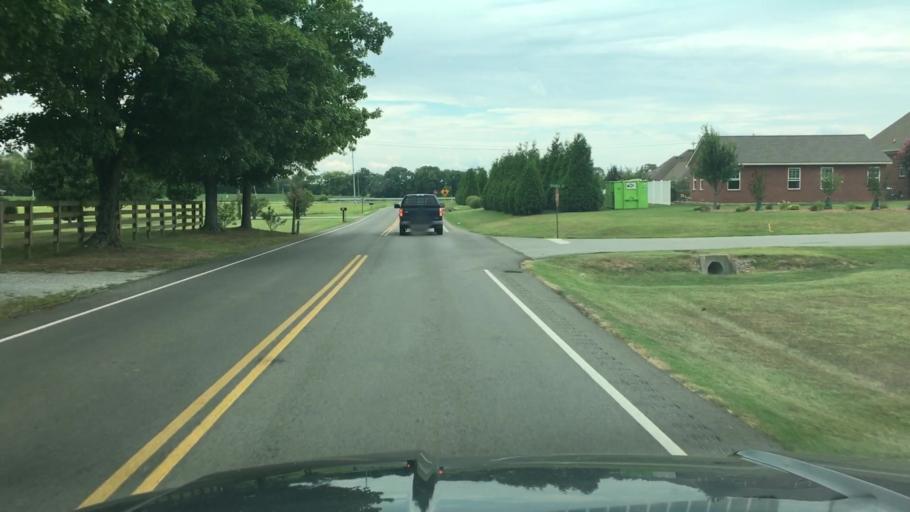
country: US
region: Tennessee
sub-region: Williamson County
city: Thompson's Station
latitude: 35.7920
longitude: -86.8642
